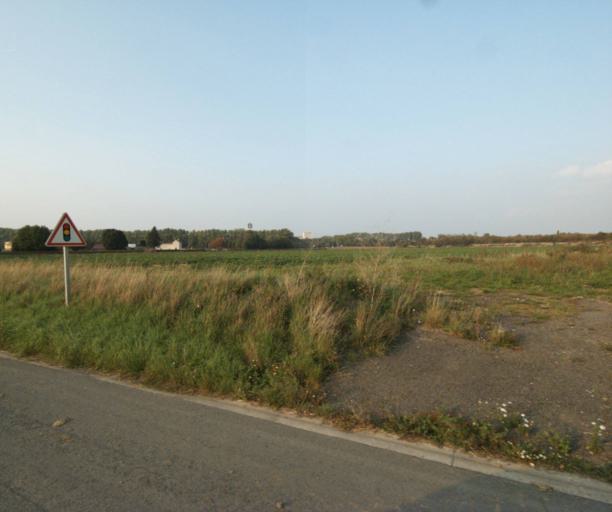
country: FR
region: Nord-Pas-de-Calais
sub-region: Departement du Nord
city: Emmerin
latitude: 50.5955
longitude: 3.0075
